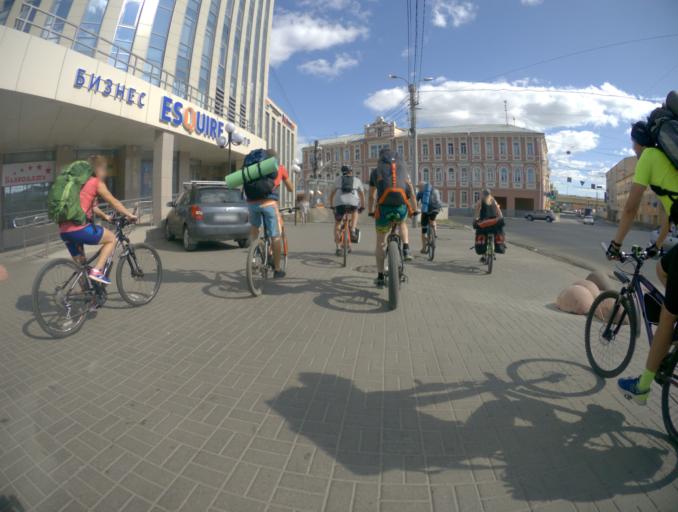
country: RU
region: Nizjnij Novgorod
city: Nizhniy Novgorod
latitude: 56.3240
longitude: 43.9525
